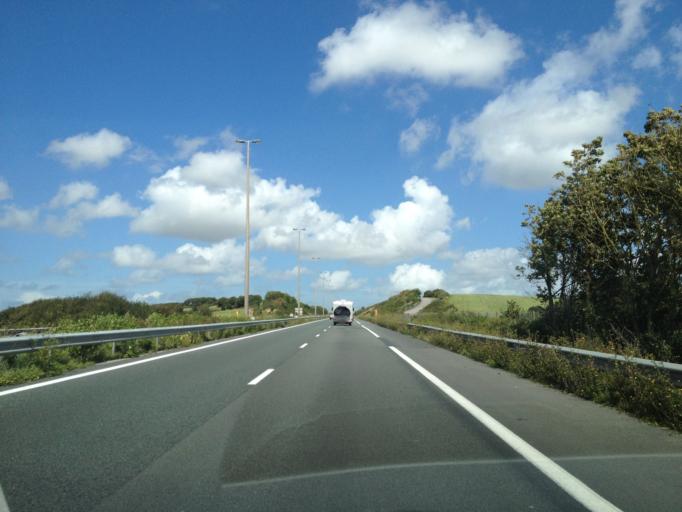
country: FR
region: Nord-Pas-de-Calais
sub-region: Departement du Pas-de-Calais
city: Marquise
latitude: 50.8354
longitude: 1.7055
